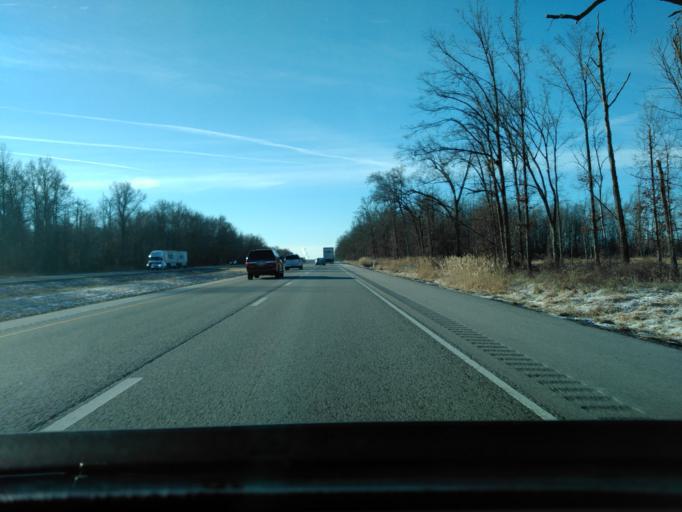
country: US
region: Illinois
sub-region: Williamson County
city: Johnston City
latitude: 37.8342
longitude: -88.9451
